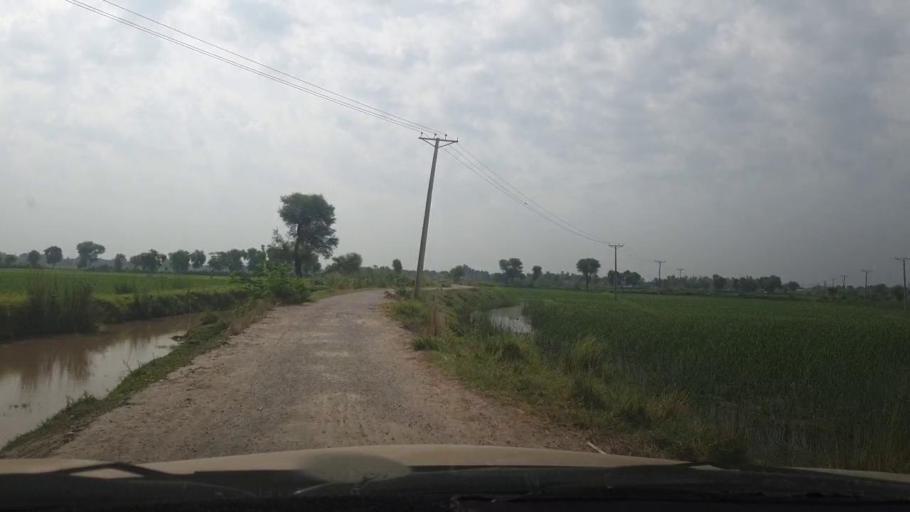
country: PK
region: Sindh
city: Larkana
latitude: 27.6425
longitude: 68.2016
